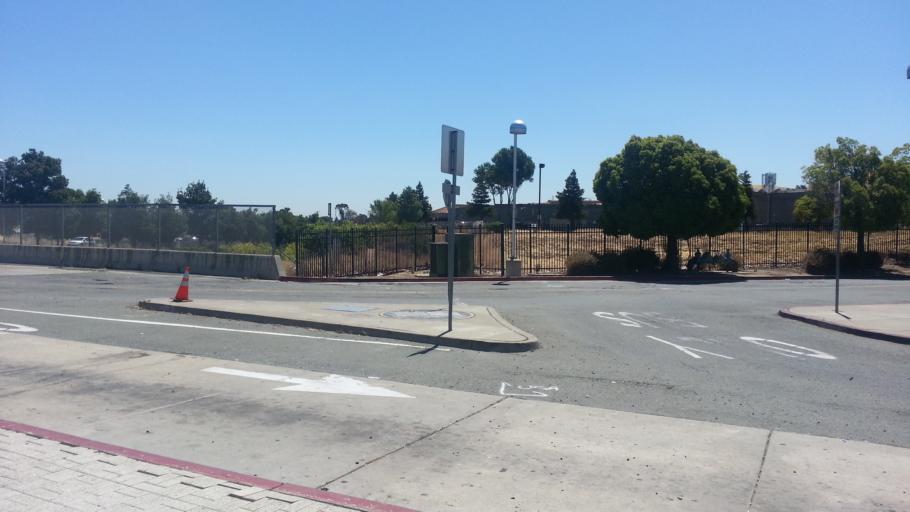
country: US
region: California
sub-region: Contra Costa County
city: Bay Point
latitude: 38.0182
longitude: -121.9450
